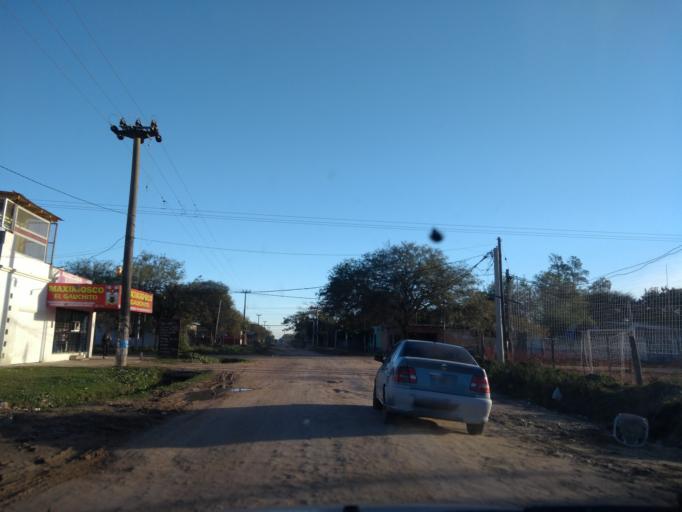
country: AR
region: Chaco
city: Puerto Vilelas
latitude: -27.4987
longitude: -58.9681
